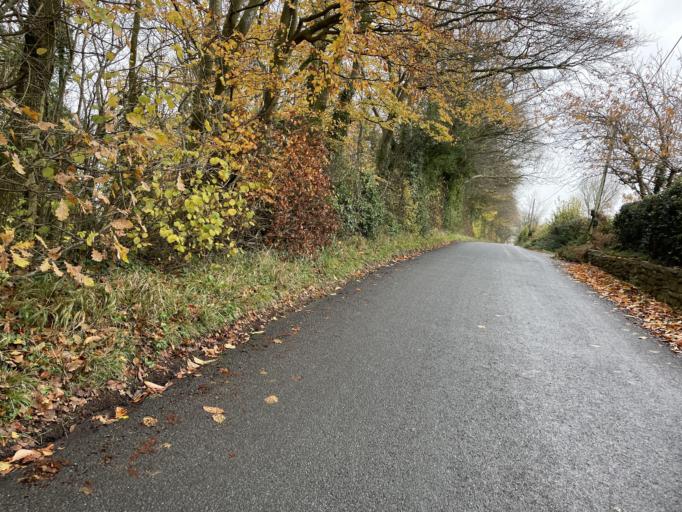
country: GB
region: England
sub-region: Herefordshire
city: Linton
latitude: 51.9247
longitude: -2.4943
